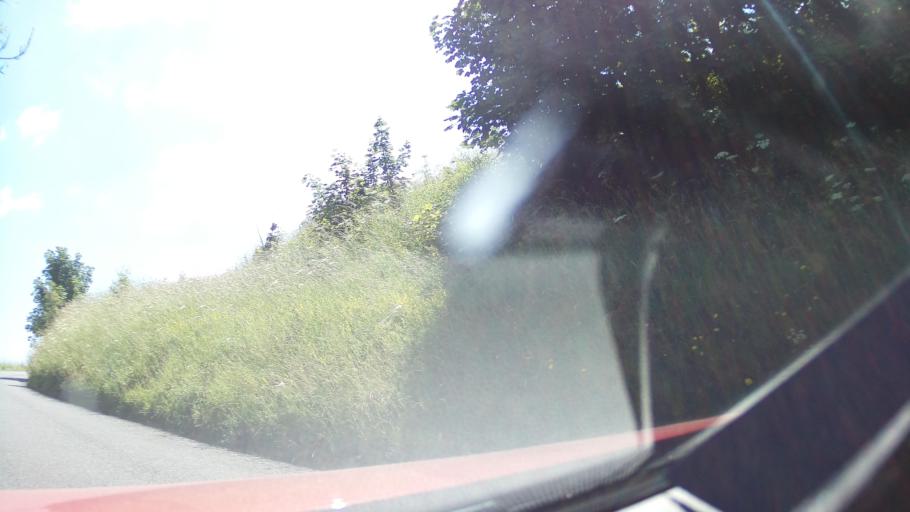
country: GB
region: England
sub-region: Derbyshire
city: Tideswell
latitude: 53.2350
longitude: -1.7872
